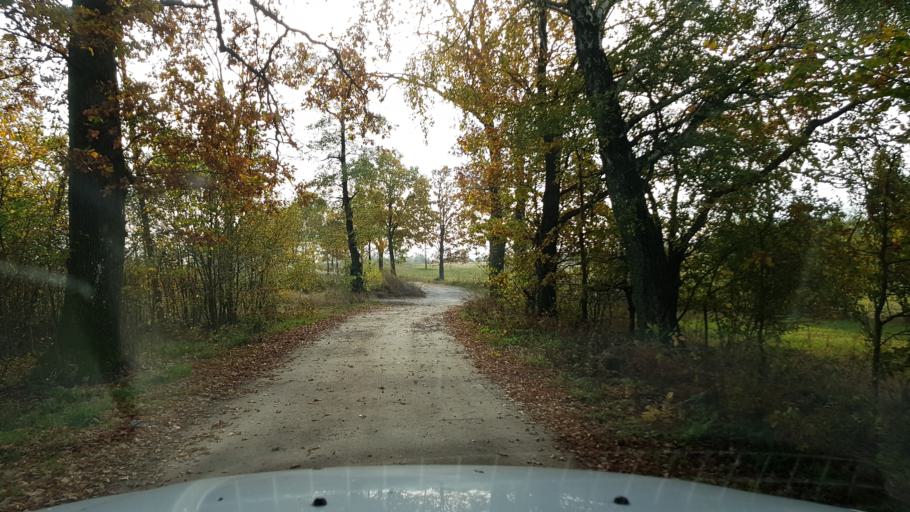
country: PL
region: West Pomeranian Voivodeship
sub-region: Powiat swidwinski
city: Polczyn-Zdroj
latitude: 53.7512
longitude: 16.0323
